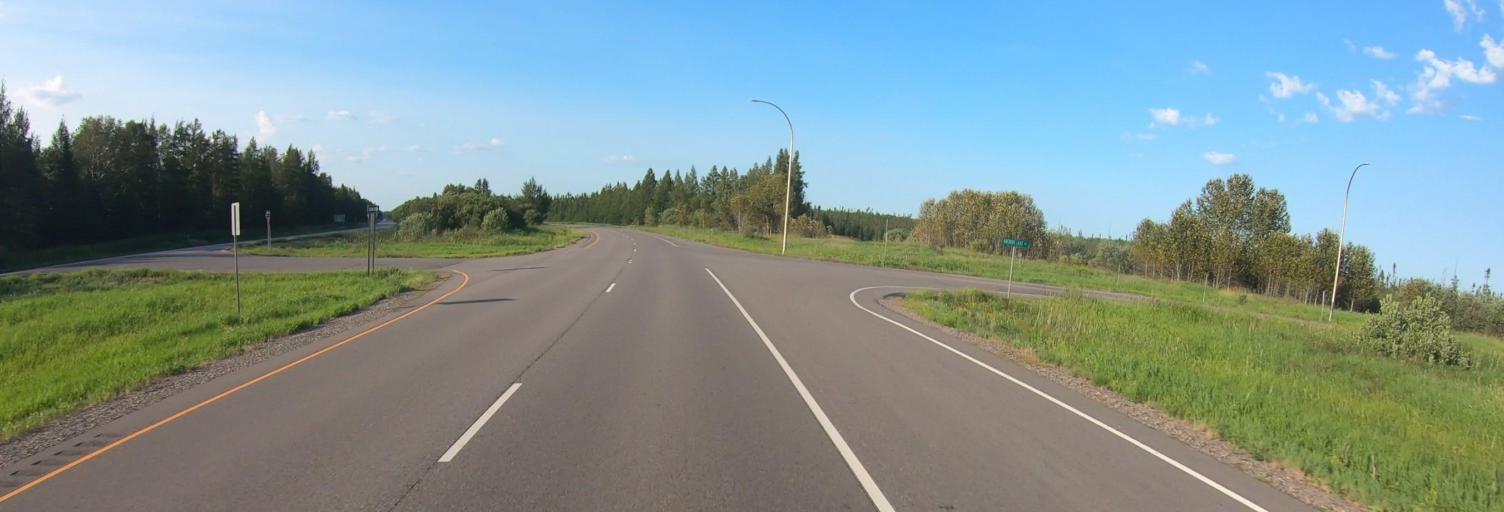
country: US
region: Minnesota
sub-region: Saint Louis County
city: Eveleth
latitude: 47.3228
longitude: -92.4696
